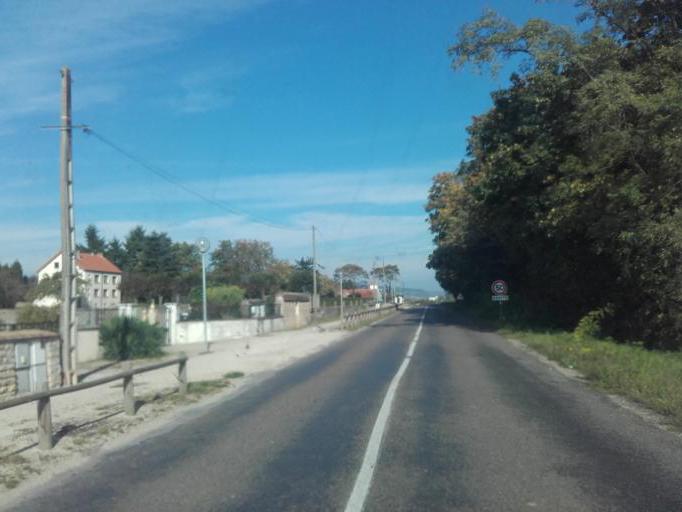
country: FR
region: Bourgogne
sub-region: Departement de Saone-et-Loire
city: Chagny
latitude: 46.8981
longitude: 4.7522
